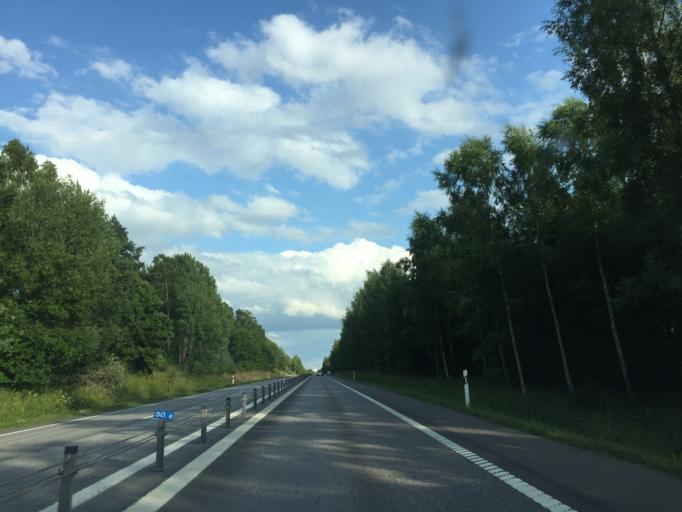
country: SE
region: OEstergoetland
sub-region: Motala Kommun
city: Motala
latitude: 58.5675
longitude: 14.9958
